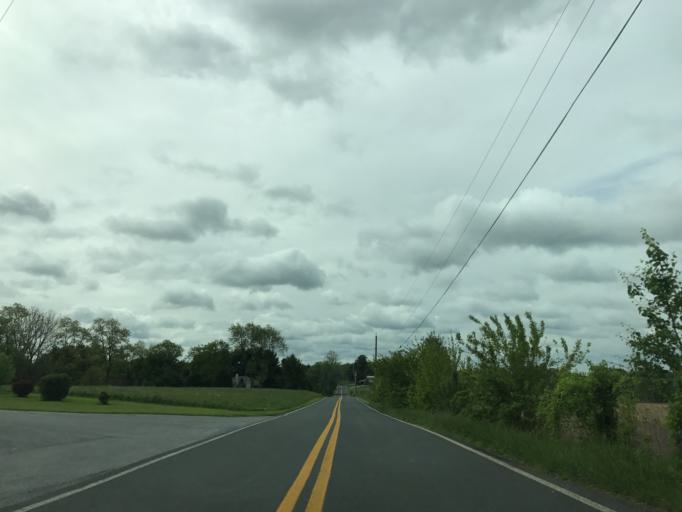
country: US
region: Maryland
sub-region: Carroll County
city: Hampstead
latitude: 39.5505
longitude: -76.8801
